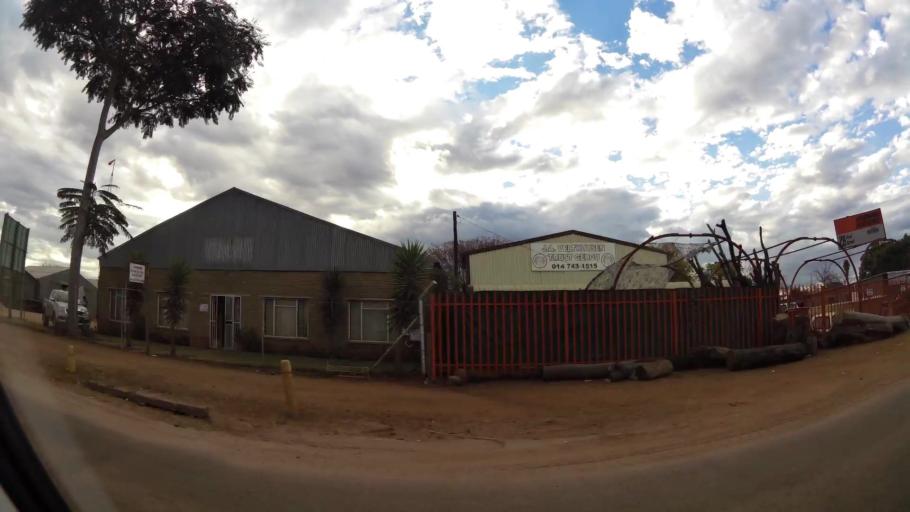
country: ZA
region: Limpopo
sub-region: Waterberg District Municipality
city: Modimolle
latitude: -24.5250
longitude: 28.7121
